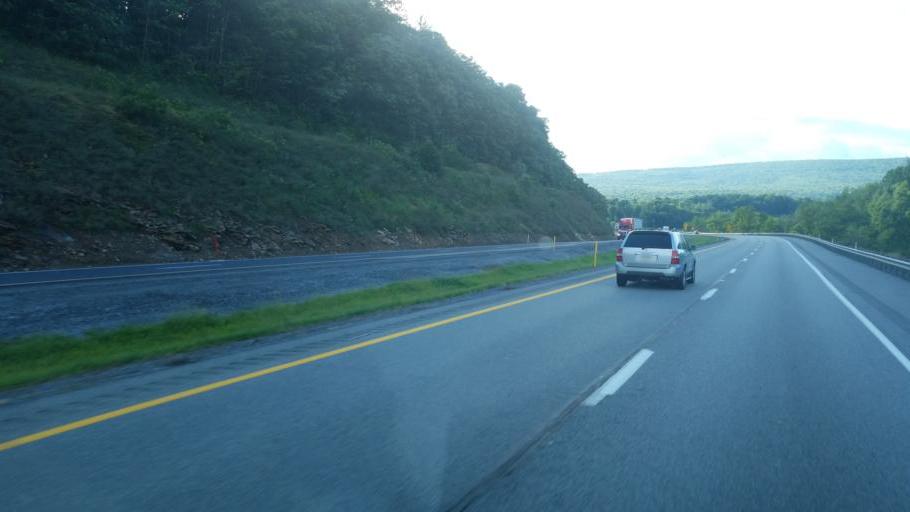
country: US
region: Pennsylvania
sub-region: Bedford County
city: Earlston
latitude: 39.9514
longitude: -78.2369
